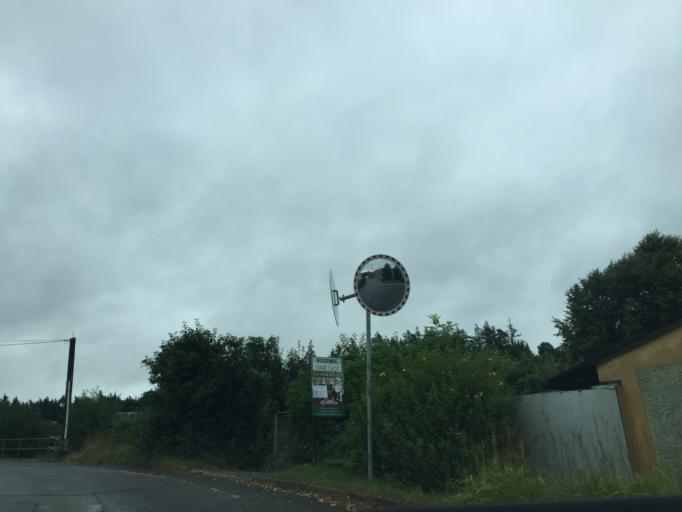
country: CZ
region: South Moravian
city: Ostrov u Macochy
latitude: 49.3786
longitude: 16.7645
